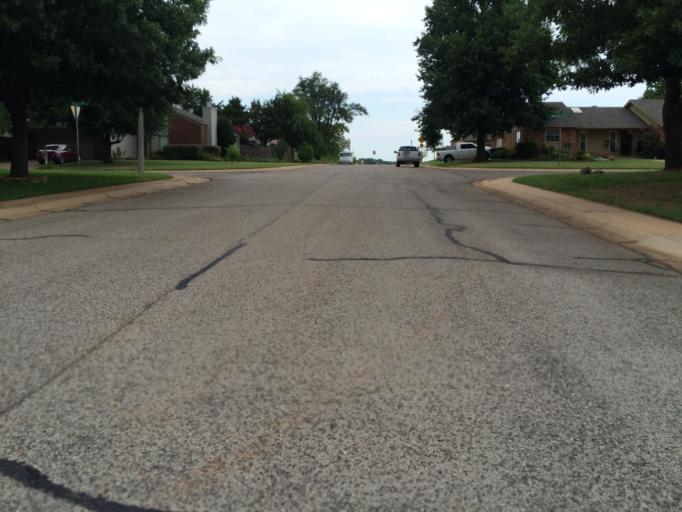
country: US
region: Oklahoma
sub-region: Cleveland County
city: Hall Park
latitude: 35.2396
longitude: -97.4132
